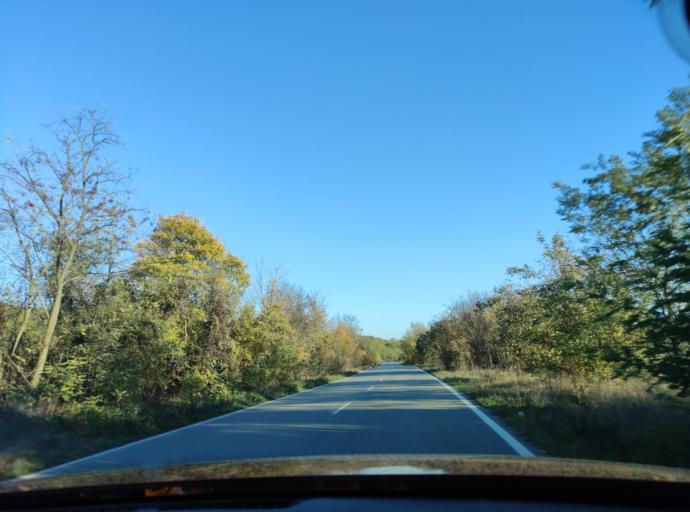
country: BG
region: Montana
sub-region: Obshtina Chiprovtsi
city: Chiprovtsi
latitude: 43.4126
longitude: 23.0420
